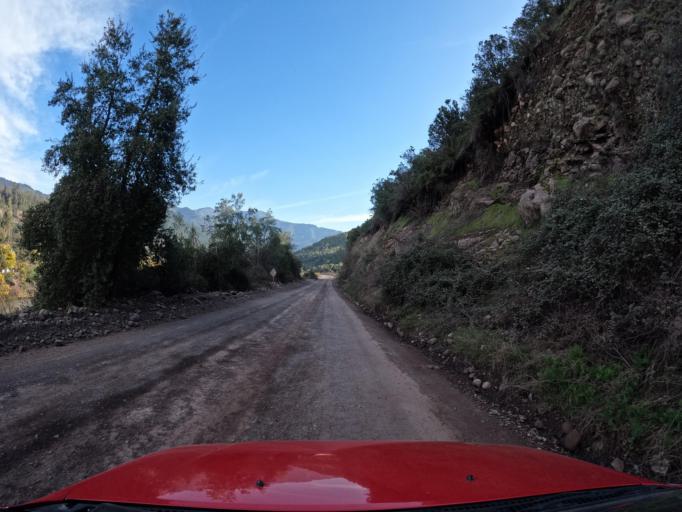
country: CL
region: O'Higgins
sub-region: Provincia de Colchagua
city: Chimbarongo
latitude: -34.9970
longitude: -70.8234
